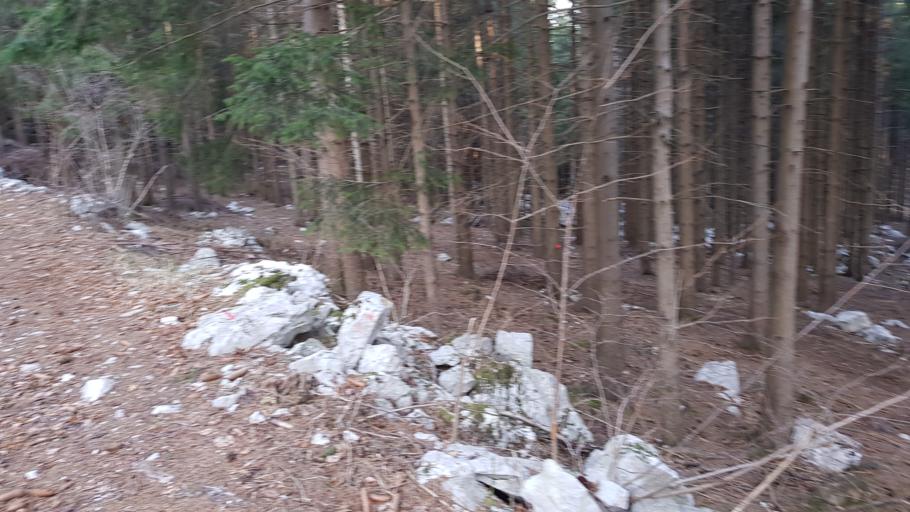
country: SI
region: Kanal
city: Kanal
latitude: 46.0335
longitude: 13.6863
